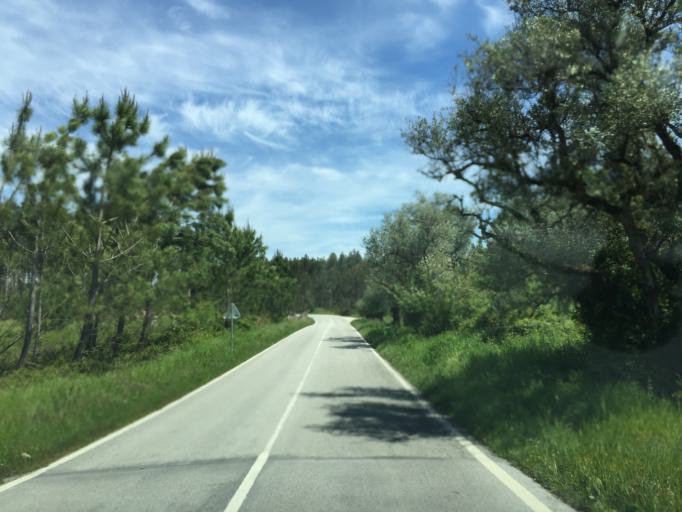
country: PT
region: Coimbra
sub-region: Soure
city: Soure
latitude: 40.0554
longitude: -8.6619
